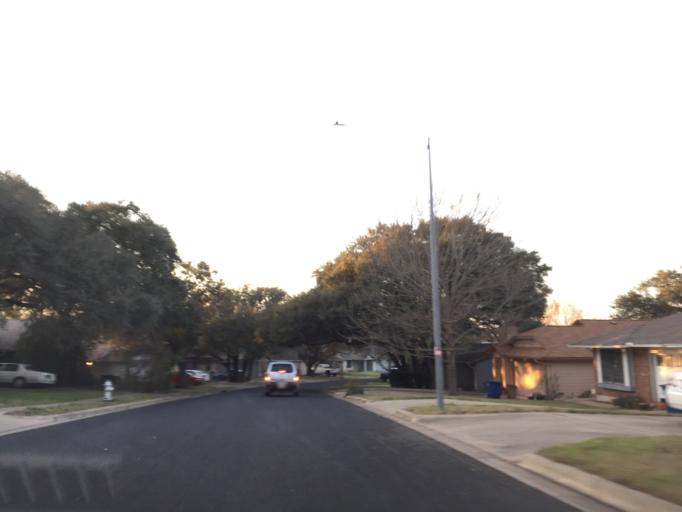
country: US
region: Texas
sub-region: Williamson County
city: Jollyville
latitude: 30.4375
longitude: -97.7390
